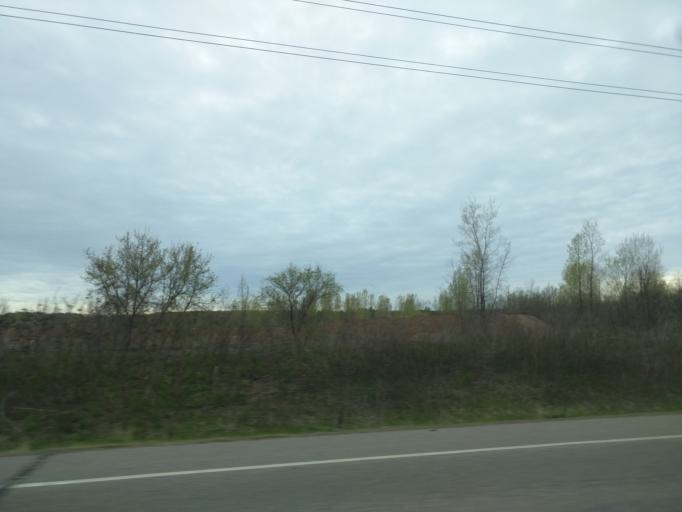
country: US
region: Minnesota
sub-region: Goodhue County
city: Red Wing
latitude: 44.6168
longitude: -92.5632
